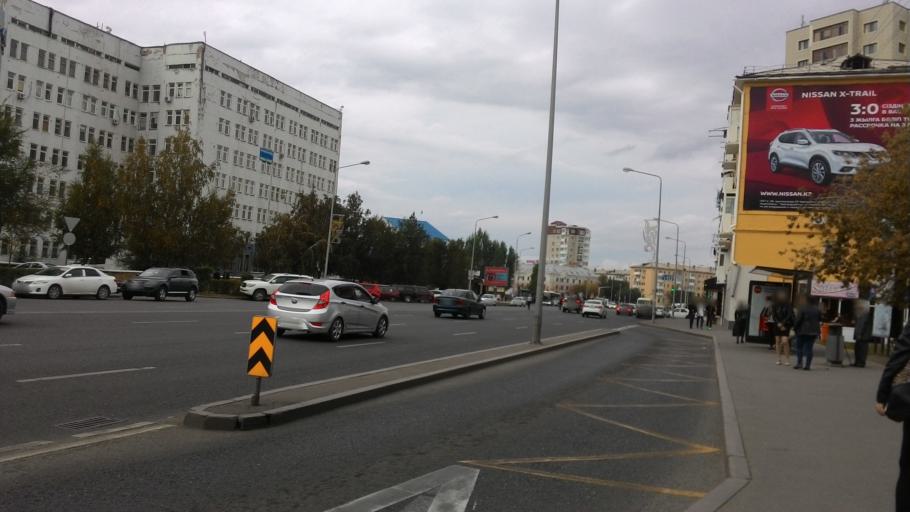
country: KZ
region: Astana Qalasy
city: Astana
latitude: 51.1892
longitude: 71.4075
